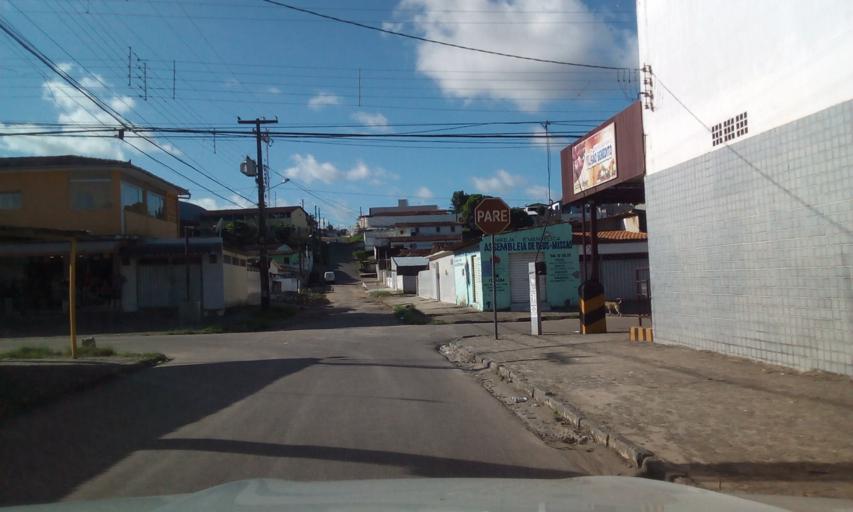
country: BR
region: Paraiba
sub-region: Joao Pessoa
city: Joao Pessoa
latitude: -7.1550
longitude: -34.8925
